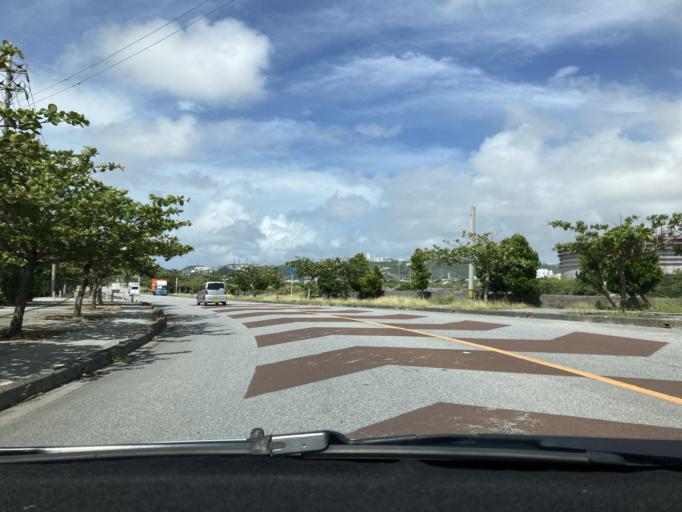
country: JP
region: Okinawa
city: Ginowan
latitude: 26.2194
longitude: 127.7775
